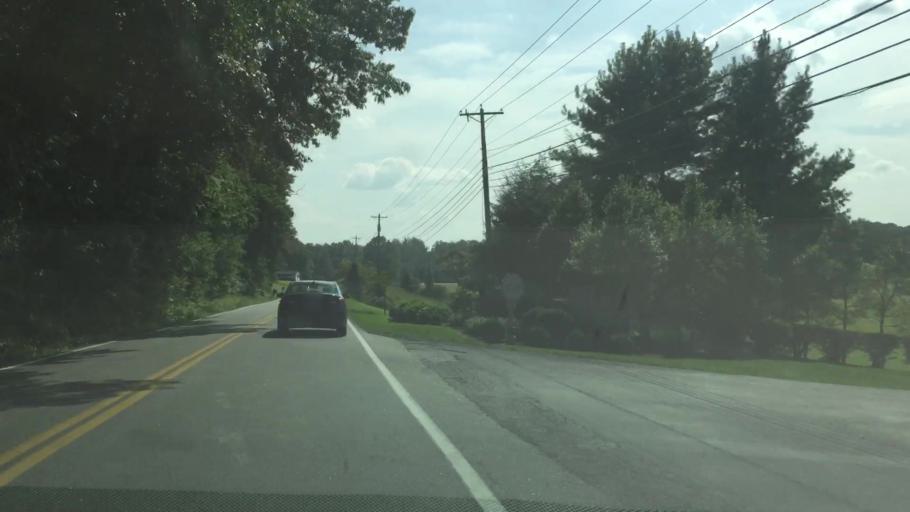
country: US
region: Tennessee
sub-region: Sullivan County
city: Fairmount
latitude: 36.6149
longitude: -82.0876
